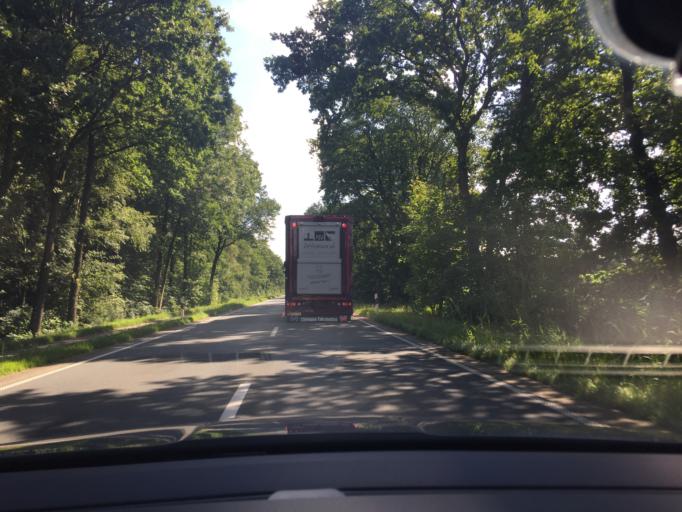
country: DE
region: Lower Saxony
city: Wittmund
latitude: 53.5643
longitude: 7.7241
